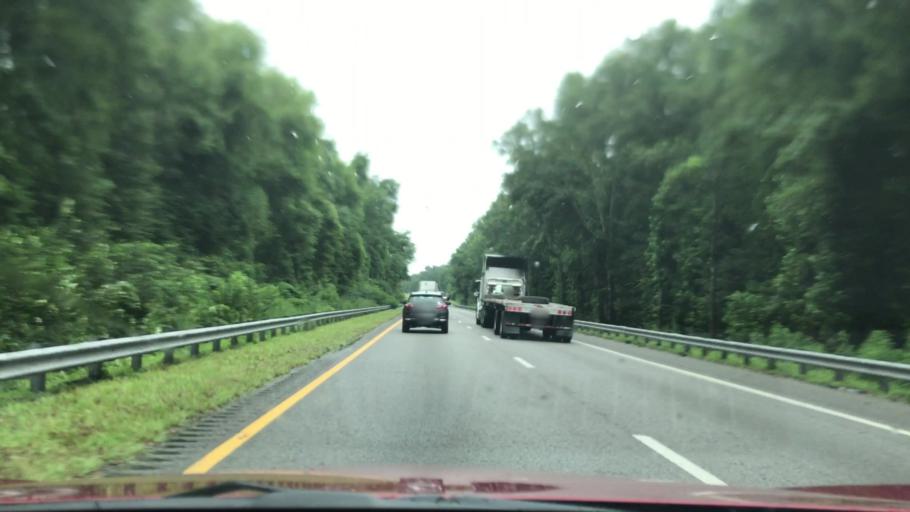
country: US
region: South Carolina
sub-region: Dorchester County
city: Ridgeville
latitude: 33.0964
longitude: -80.2360
